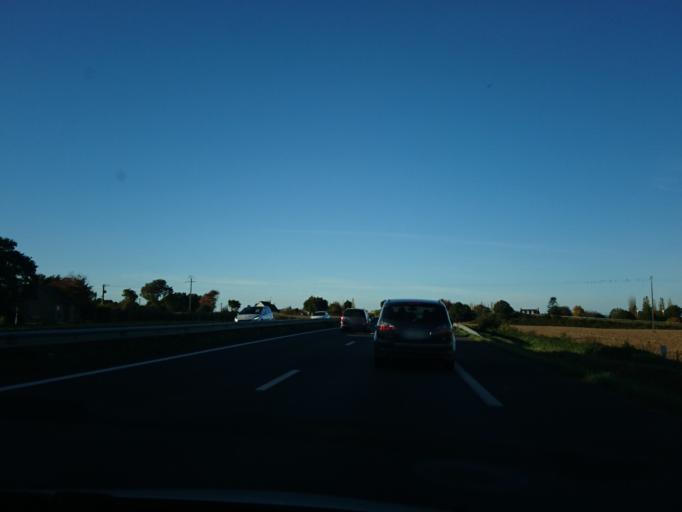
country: FR
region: Brittany
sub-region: Departement des Cotes-d'Armor
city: Plestan
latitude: 48.4415
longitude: -2.4774
